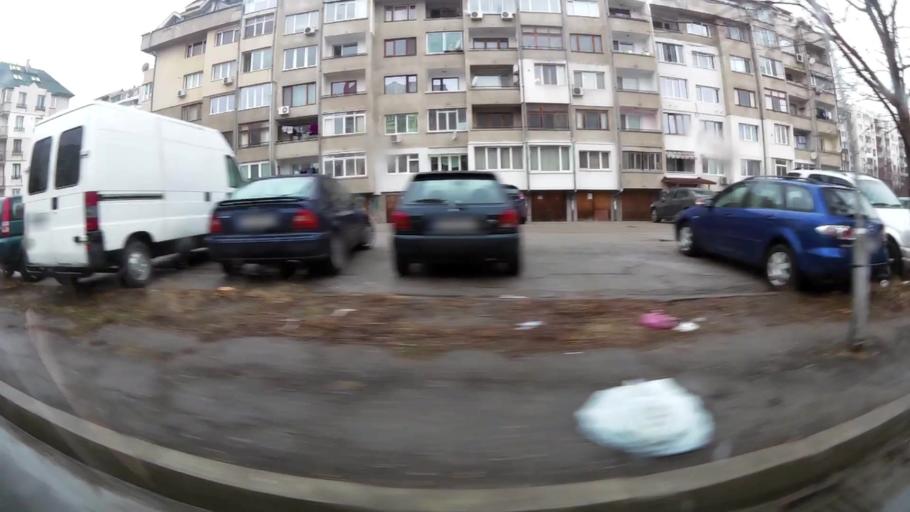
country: BG
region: Sofia-Capital
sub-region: Stolichna Obshtina
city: Sofia
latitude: 42.6379
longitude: 23.3763
